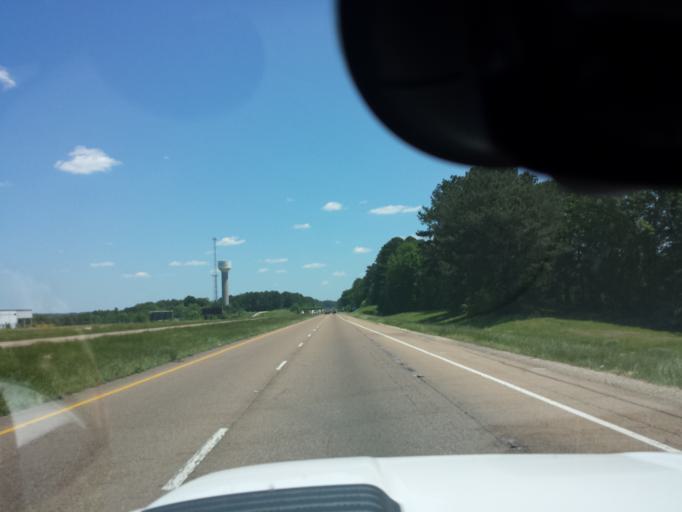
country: US
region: Mississippi
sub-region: Lauderdale County
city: Marion
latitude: 32.3844
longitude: -88.6297
